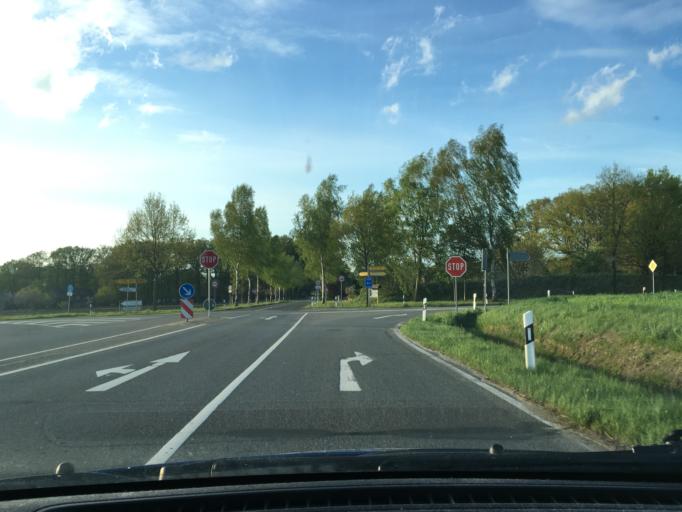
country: DE
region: Lower Saxony
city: Wietzendorf
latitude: 52.9605
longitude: 9.9733
